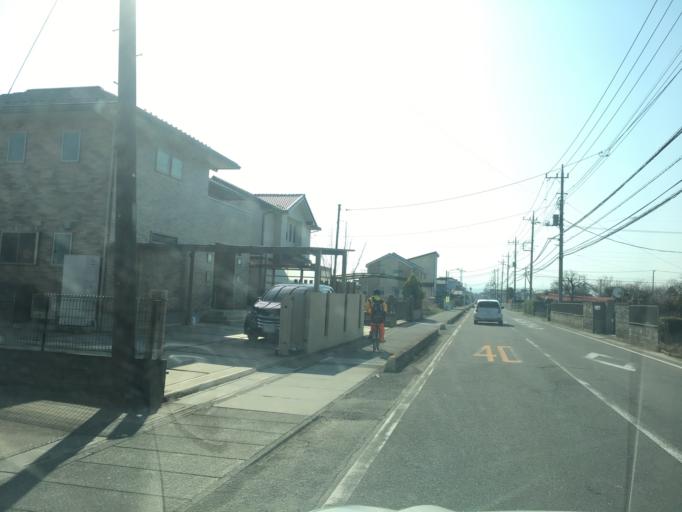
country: JP
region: Saitama
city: Kawagoe
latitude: 35.9270
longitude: 139.5043
